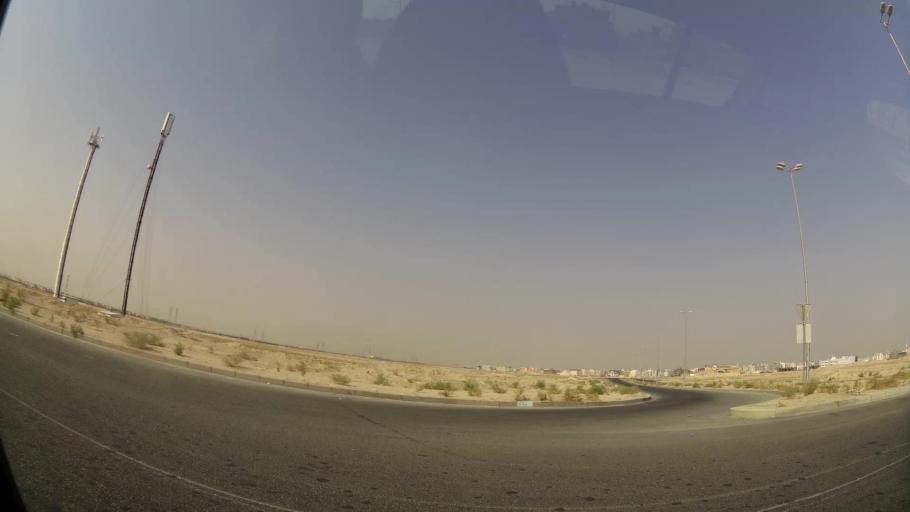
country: KW
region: Muhafazat al Jahra'
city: Al Jahra'
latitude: 29.3376
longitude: 47.7593
